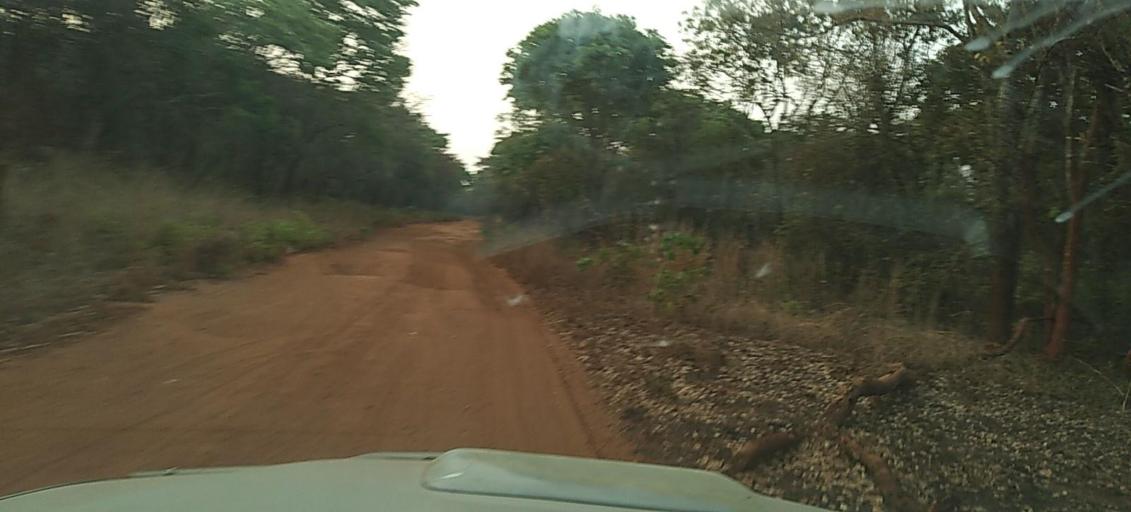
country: ZM
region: North-Western
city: Kasempa
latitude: -13.0893
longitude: 26.3989
